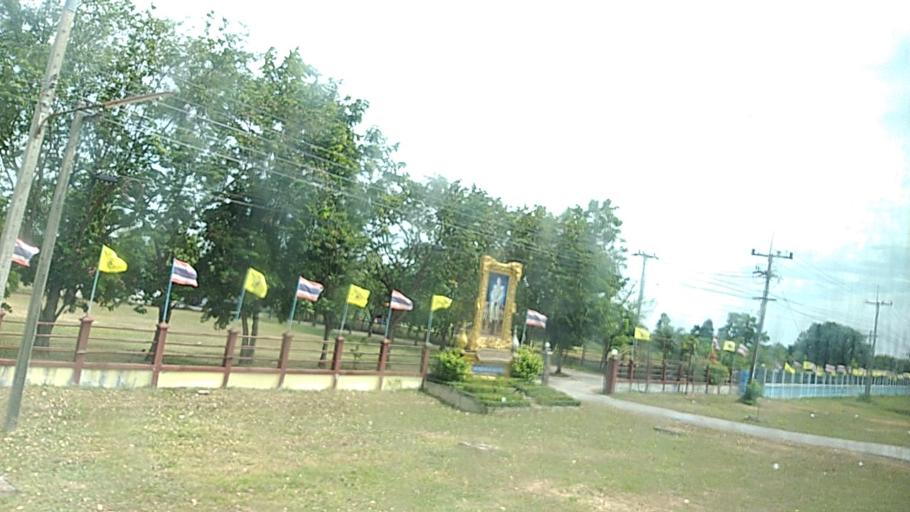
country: TH
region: Maha Sarakham
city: Chiang Yuen
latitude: 16.3631
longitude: 103.1087
